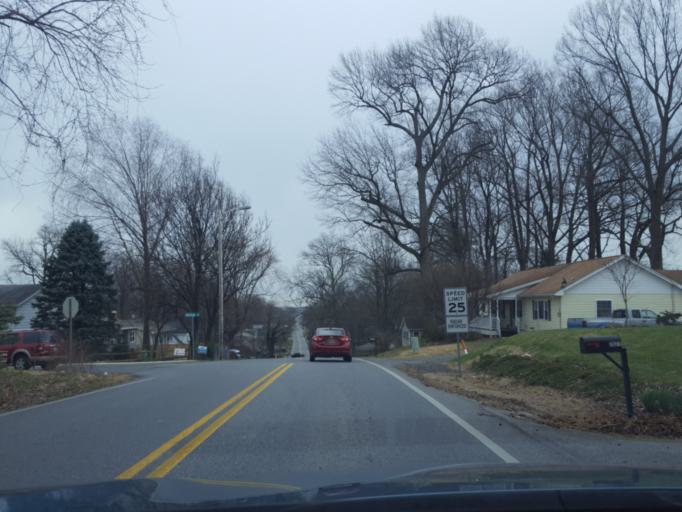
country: US
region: Maryland
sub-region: Calvert County
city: North Beach
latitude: 38.7084
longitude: -76.5442
